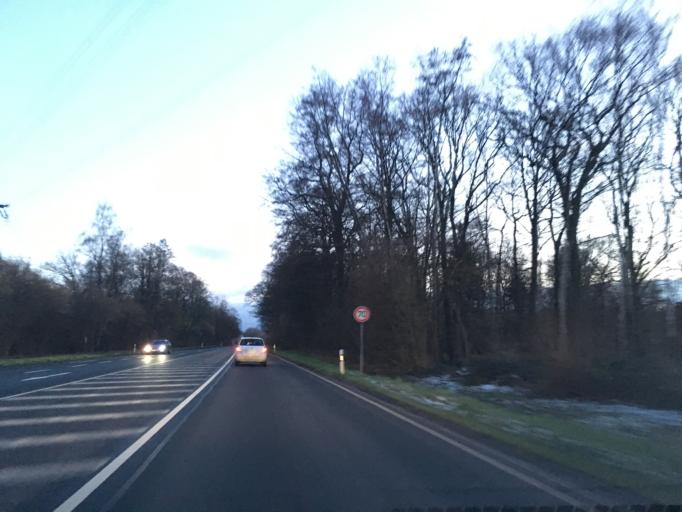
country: DE
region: North Rhine-Westphalia
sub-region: Regierungsbezirk Munster
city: Muenster
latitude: 51.8855
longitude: 7.6476
